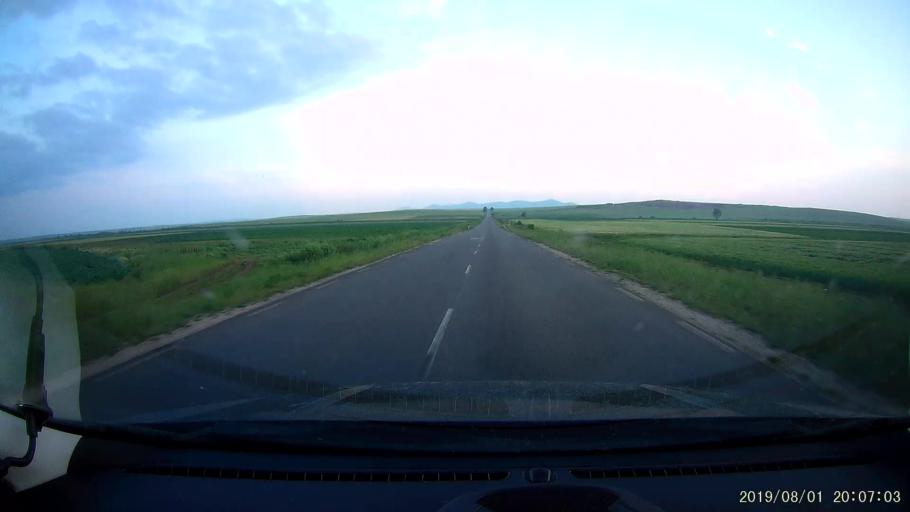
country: BG
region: Yambol
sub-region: Obshtina Yambol
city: Yambol
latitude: 42.5279
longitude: 26.5618
